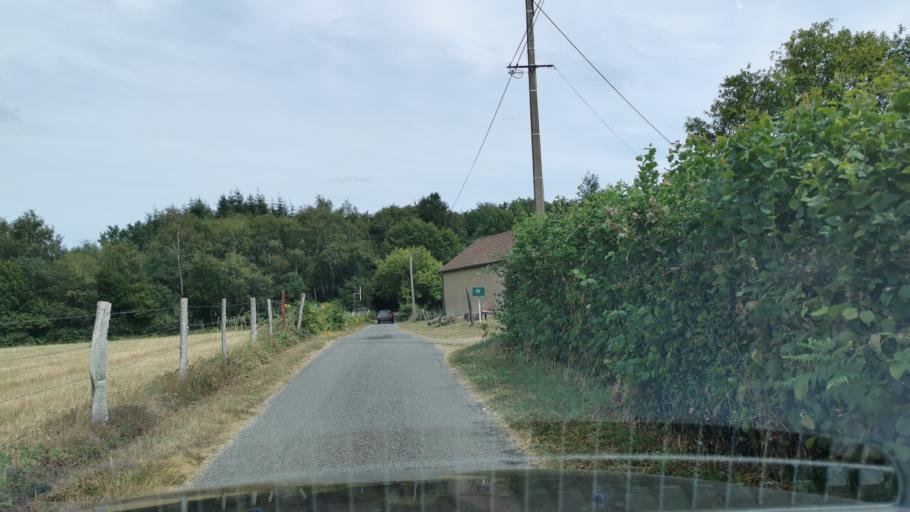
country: FR
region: Bourgogne
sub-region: Departement de Saone-et-Loire
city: Saint-Berain-sous-Sanvignes
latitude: 46.8012
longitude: 4.2666
